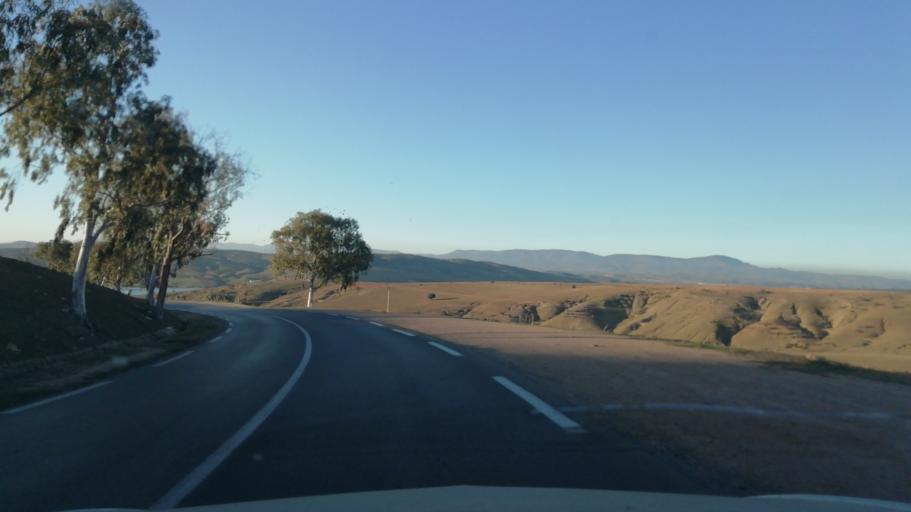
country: DZ
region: Tlemcen
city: Nedroma
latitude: 34.8276
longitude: -1.6397
